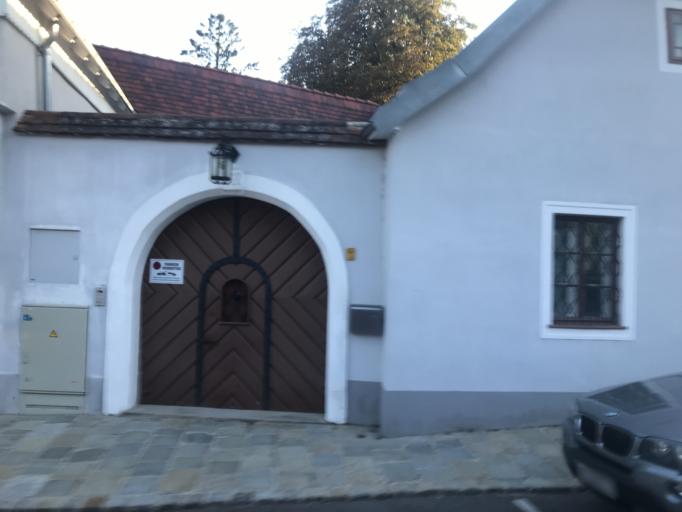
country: AT
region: Lower Austria
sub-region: Politischer Bezirk Korneuburg
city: Langenzersdorf
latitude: 48.2583
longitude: 16.3372
